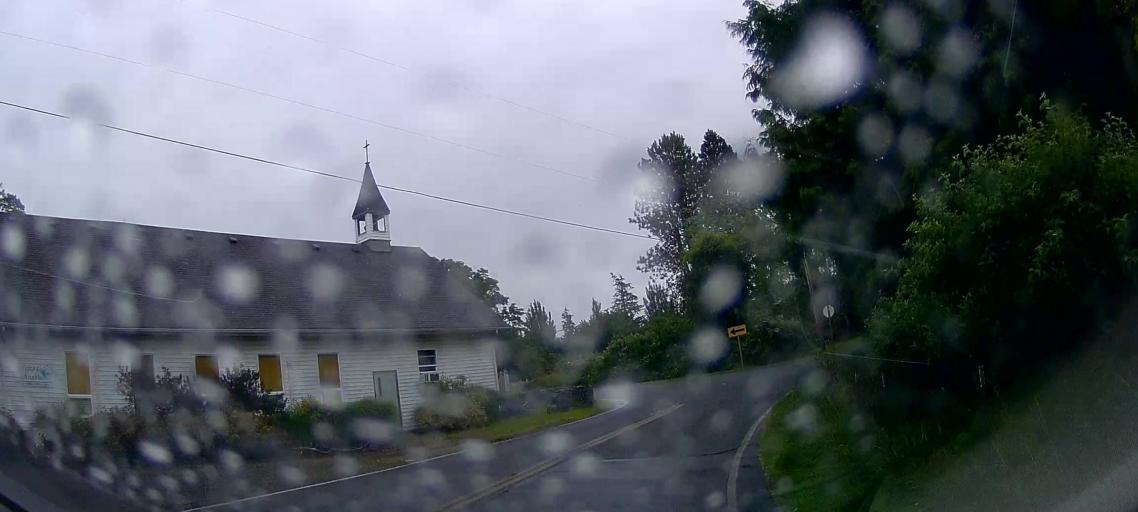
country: US
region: Washington
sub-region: Whatcom County
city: Marietta
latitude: 48.7934
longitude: -122.5786
